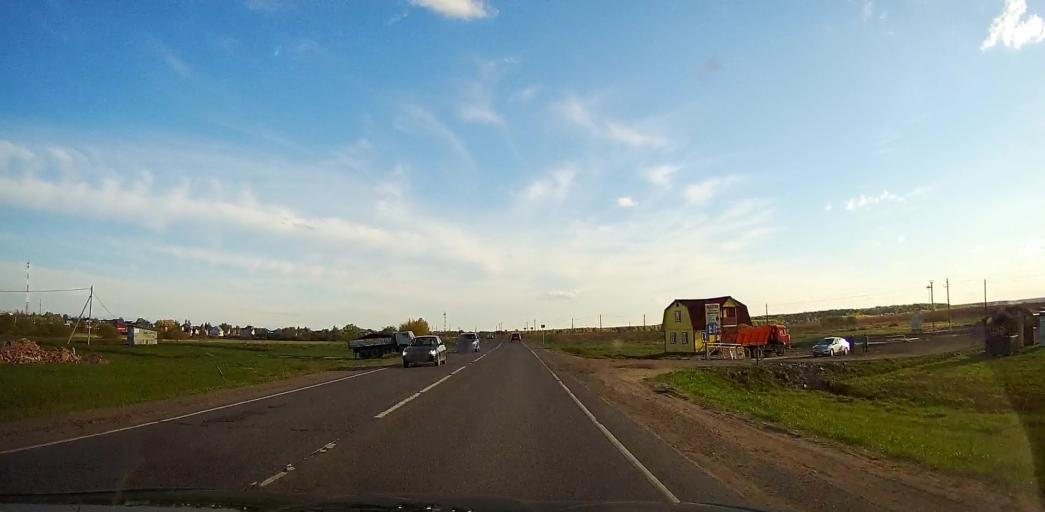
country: RU
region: Moskovskaya
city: Bronnitsy
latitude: 55.3352
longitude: 38.2202
